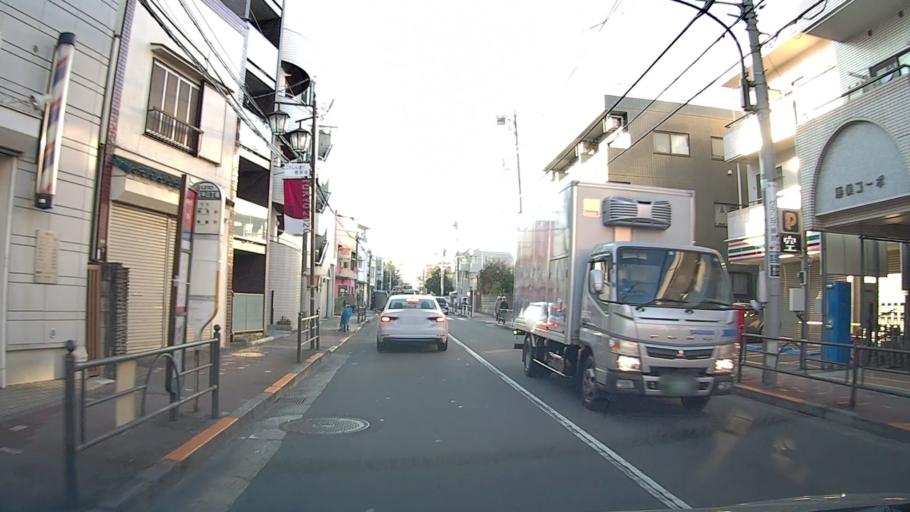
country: JP
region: Tokyo
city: Tokyo
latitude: 35.7323
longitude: 139.6543
